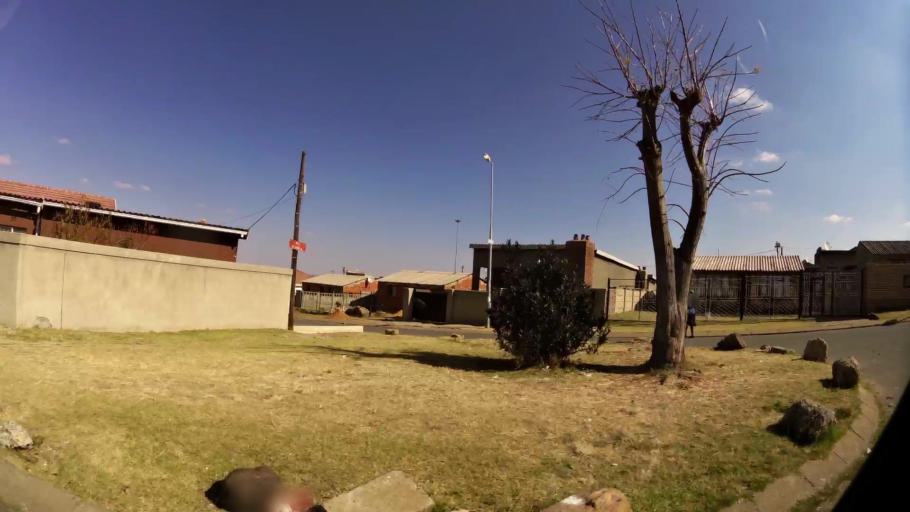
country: ZA
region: Gauteng
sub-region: City of Johannesburg Metropolitan Municipality
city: Soweto
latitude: -26.2411
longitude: 27.9022
